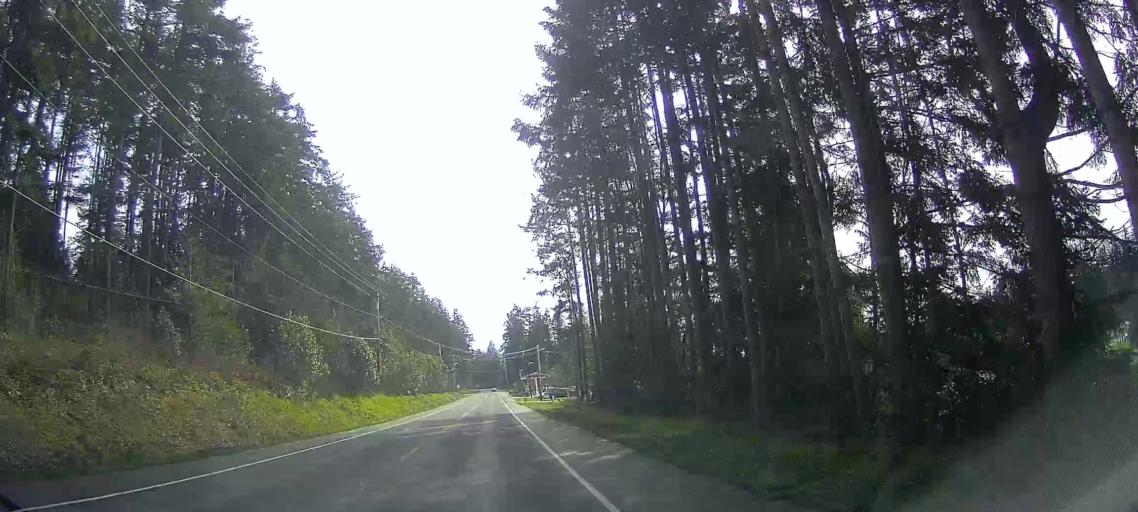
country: US
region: Washington
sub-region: Island County
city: Camano
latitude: 48.1402
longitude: -122.4678
